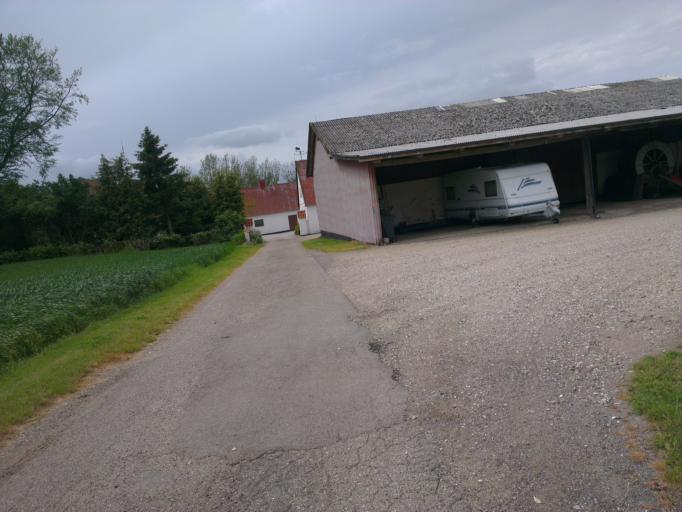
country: DK
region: Capital Region
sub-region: Frederikssund Kommune
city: Frederikssund
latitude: 55.8270
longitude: 12.1066
